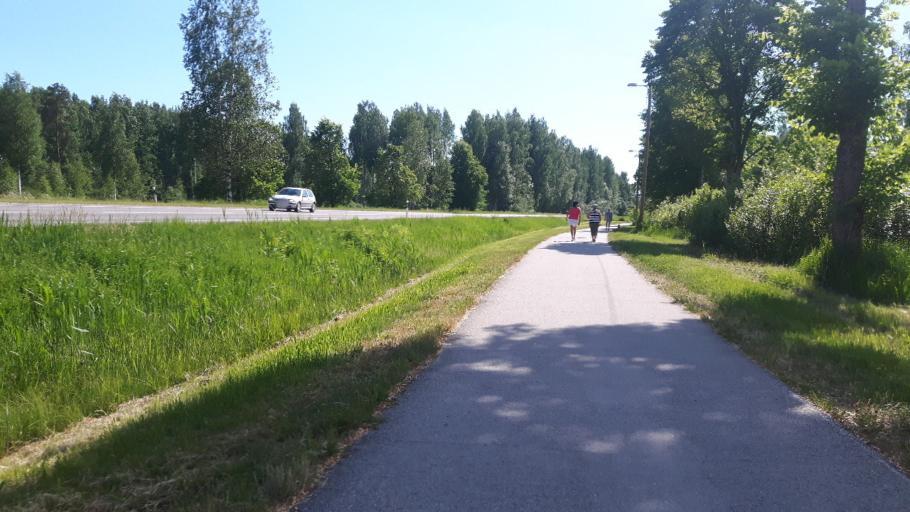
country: EE
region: Paernumaa
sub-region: Paikuse vald
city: Paikuse
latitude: 58.3855
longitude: 24.6386
